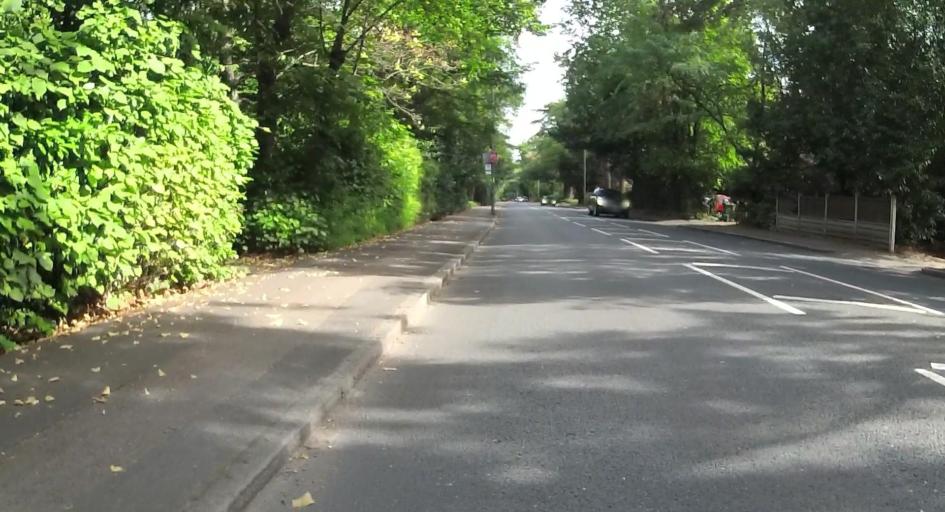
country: GB
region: England
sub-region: Surrey
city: Weybridge
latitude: 51.3657
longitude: -0.4397
